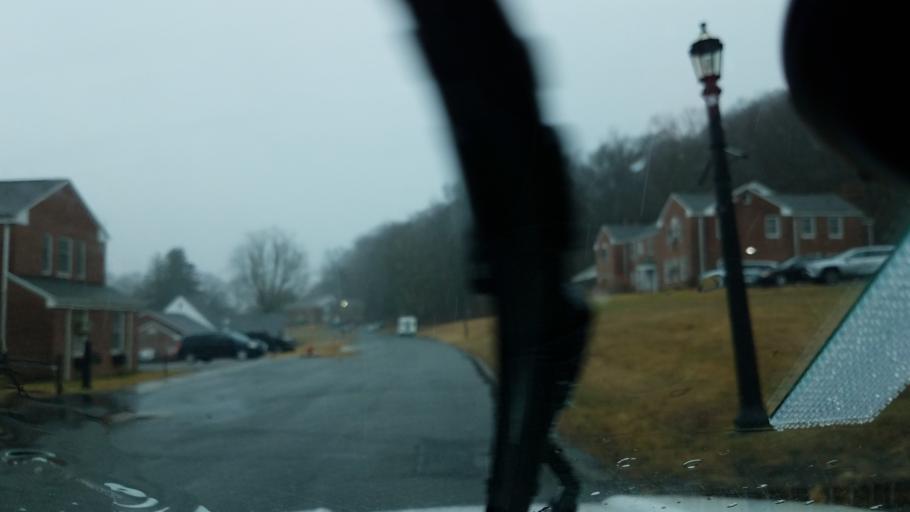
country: US
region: Connecticut
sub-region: New Haven County
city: Heritage Village
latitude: 41.4916
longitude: -73.2640
